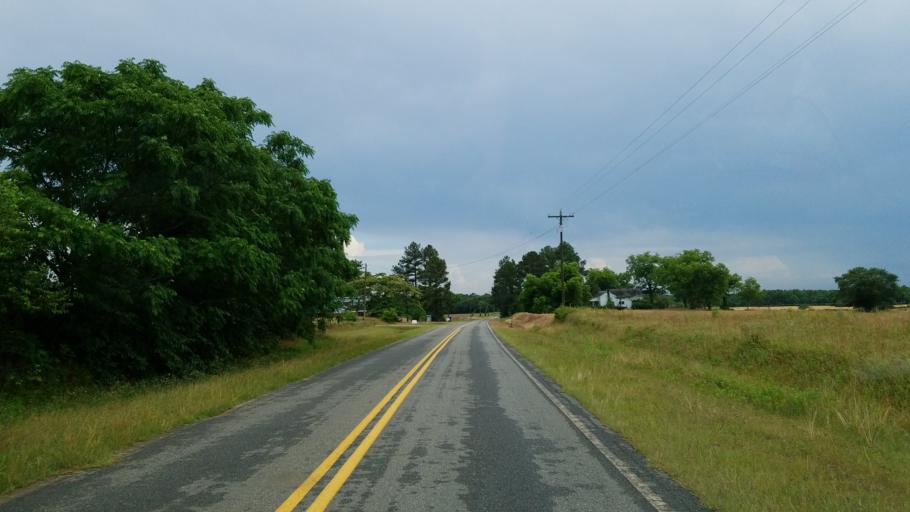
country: US
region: Georgia
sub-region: Dooly County
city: Unadilla
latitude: 32.2411
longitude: -83.7974
